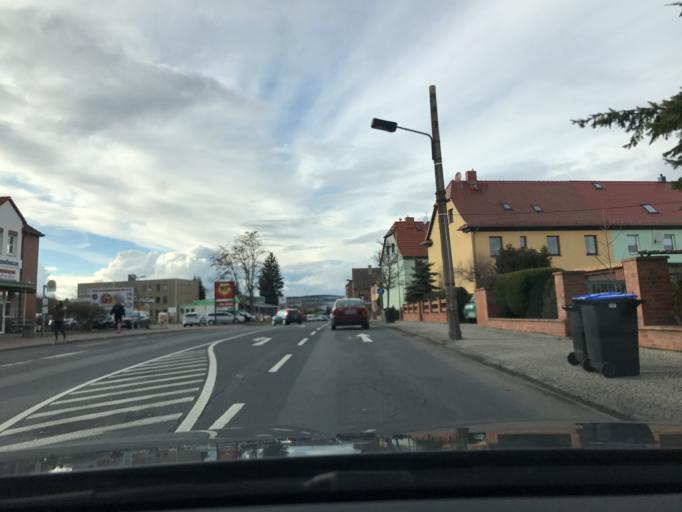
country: DE
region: Saxony-Anhalt
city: Wimmelburg
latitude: 51.5216
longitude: 11.5436
